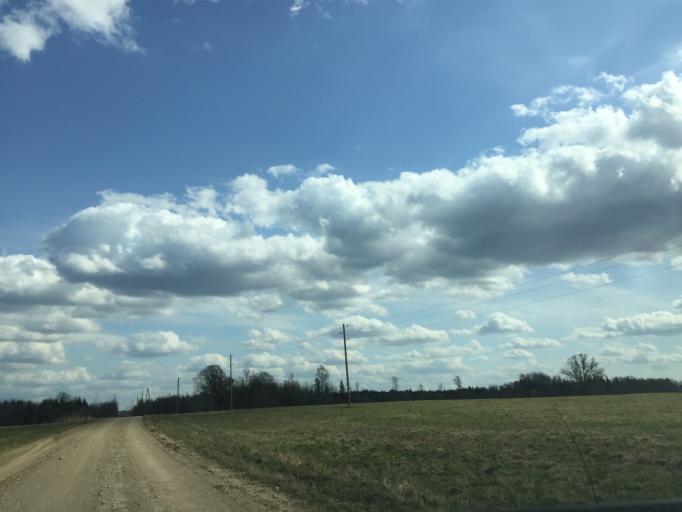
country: LV
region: Skriveri
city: Skriveri
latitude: 56.7594
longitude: 25.1548
